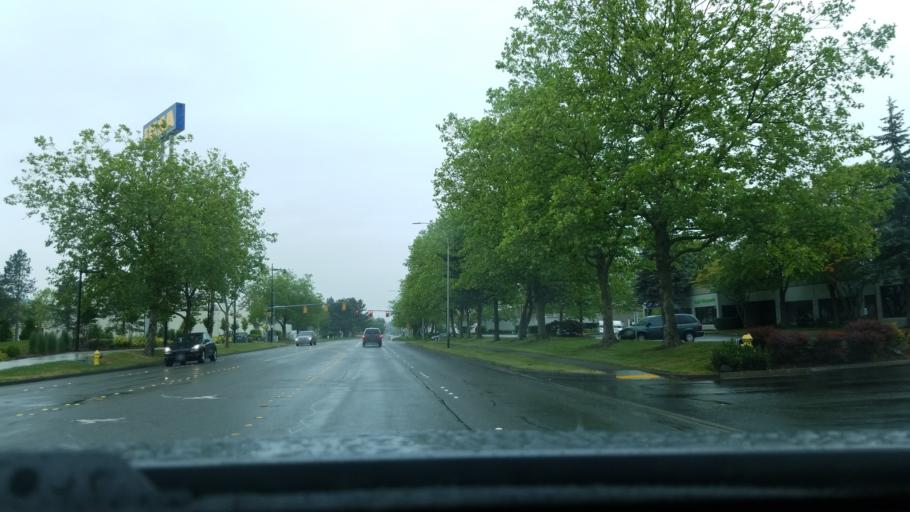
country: US
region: Washington
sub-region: King County
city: Renton
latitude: 47.4426
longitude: -122.2239
